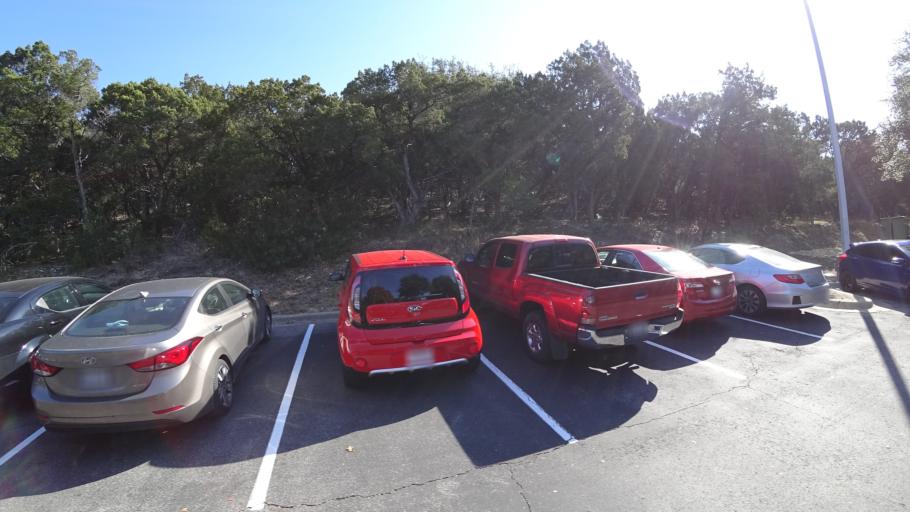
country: US
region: Texas
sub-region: Williamson County
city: Jollyville
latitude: 30.3750
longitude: -97.7800
